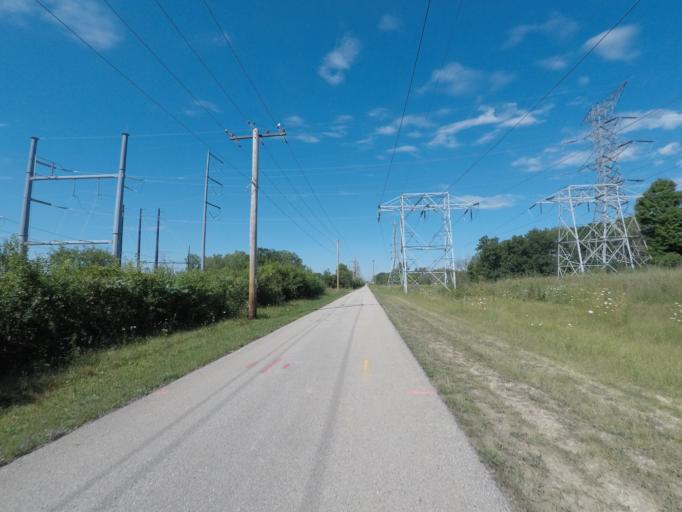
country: US
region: Wisconsin
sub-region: Waukesha County
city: Waukesha
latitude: 43.0099
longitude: -88.1738
